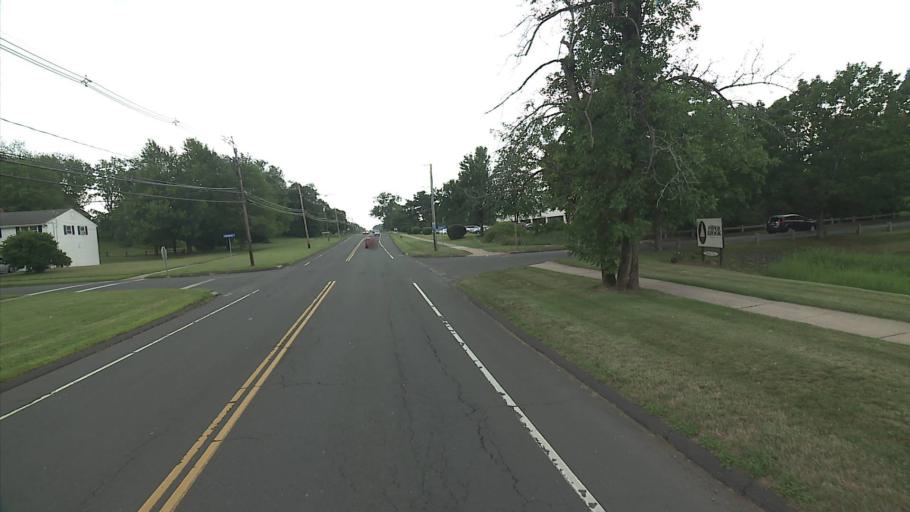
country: US
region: Connecticut
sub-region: Hartford County
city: Newington
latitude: 41.7096
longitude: -72.7364
